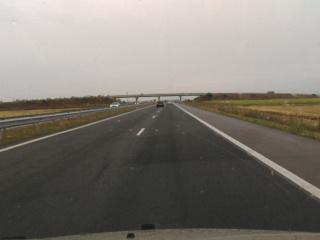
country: BG
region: Stara Zagora
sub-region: Obshtina Stara Zagora
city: Stara Zagora
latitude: 42.3666
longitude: 25.7860
